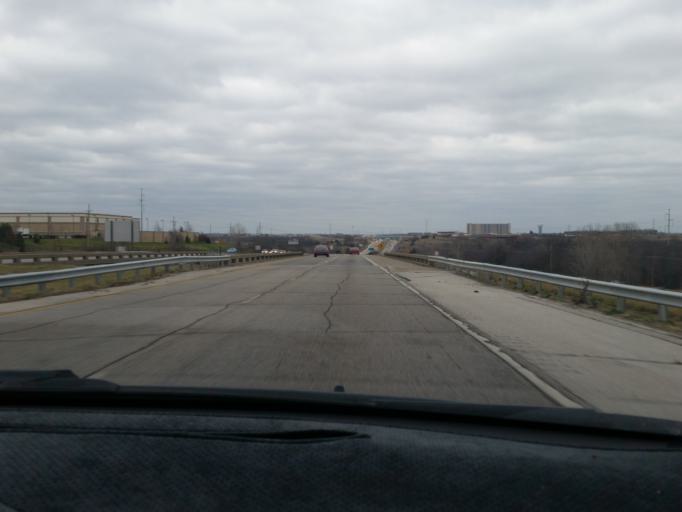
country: US
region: Kansas
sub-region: Johnson County
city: Olathe
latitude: 38.9418
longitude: -94.8170
